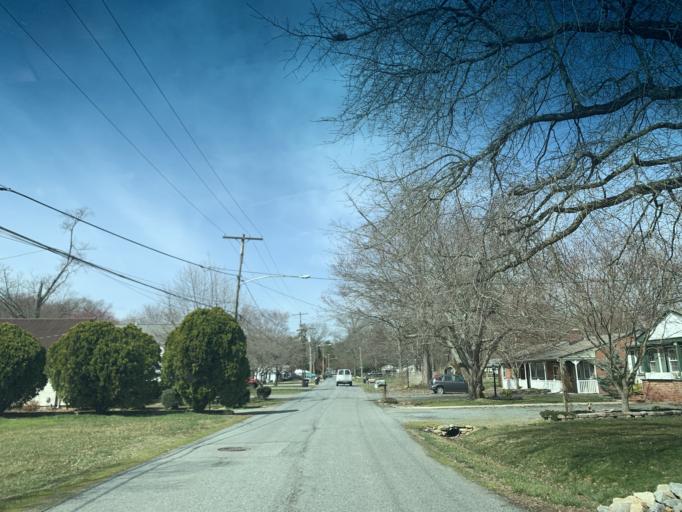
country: US
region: Maryland
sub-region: Cecil County
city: Charlestown
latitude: 39.5779
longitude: -75.9699
